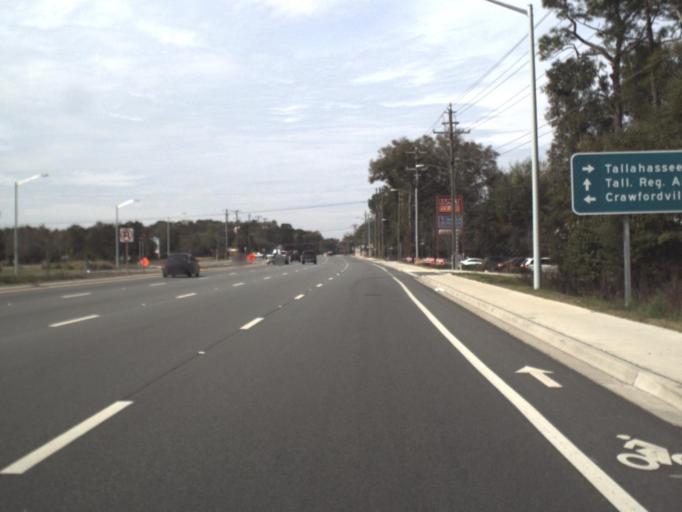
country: US
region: Florida
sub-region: Leon County
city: Tallahassee
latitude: 30.3759
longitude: -84.2877
